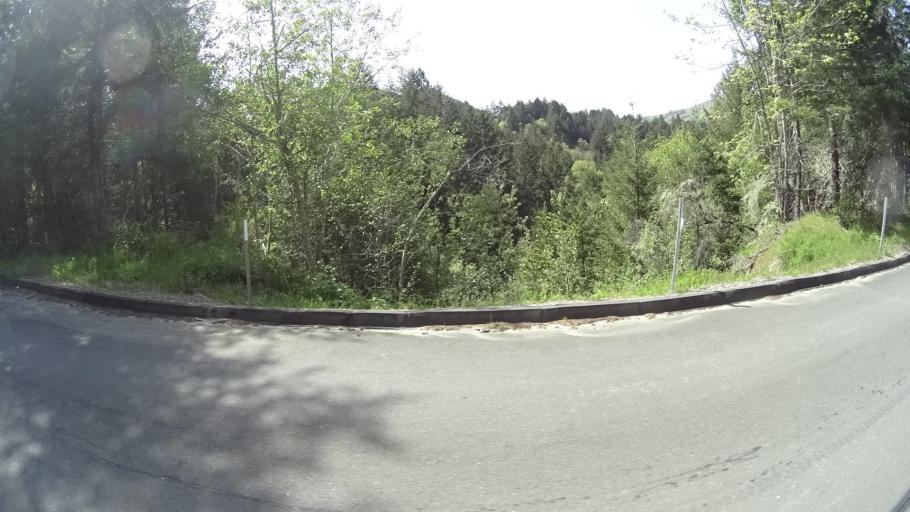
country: US
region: California
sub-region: Humboldt County
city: Rio Dell
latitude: 40.4588
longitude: -123.8043
